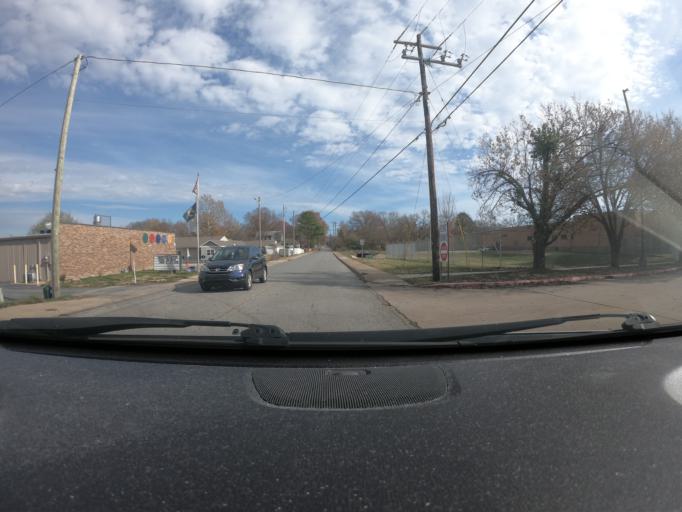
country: US
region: Arkansas
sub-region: Benton County
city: Rogers
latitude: 36.3371
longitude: -94.1253
